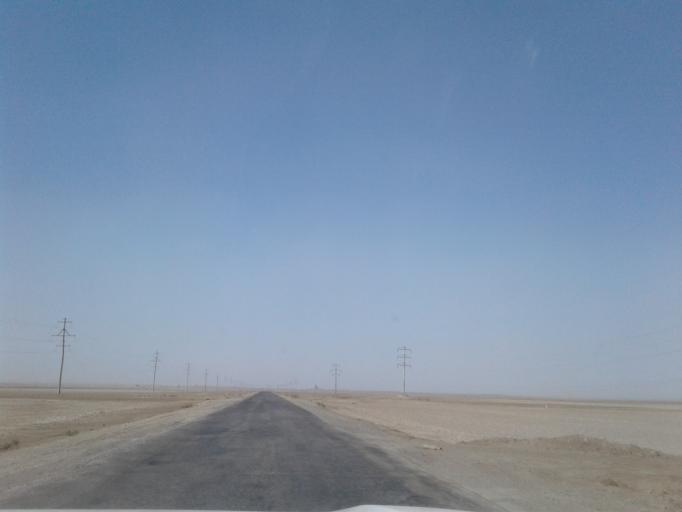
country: TM
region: Balkan
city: Gumdag
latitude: 39.0807
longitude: 54.5844
